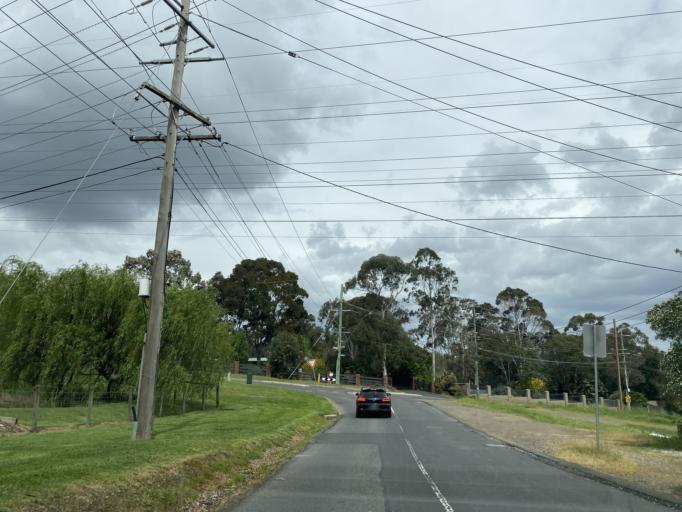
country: AU
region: Victoria
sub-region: Banyule
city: Lower Plenty
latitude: -37.7356
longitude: 145.1182
